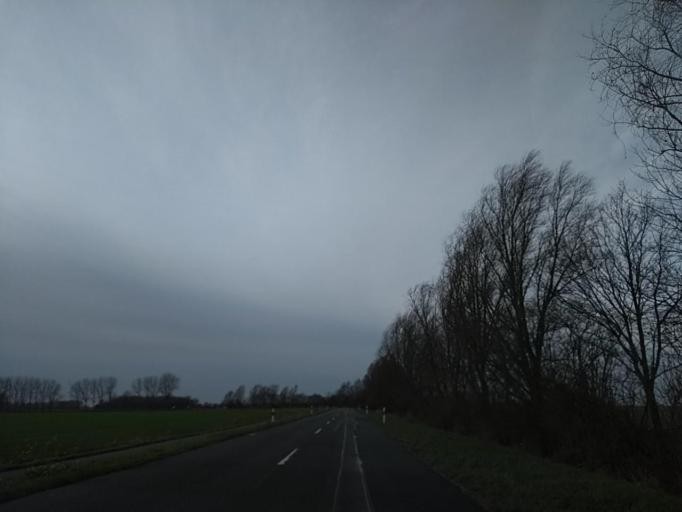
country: DE
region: Lower Saxony
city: Hinte
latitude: 53.3526
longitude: 7.0843
